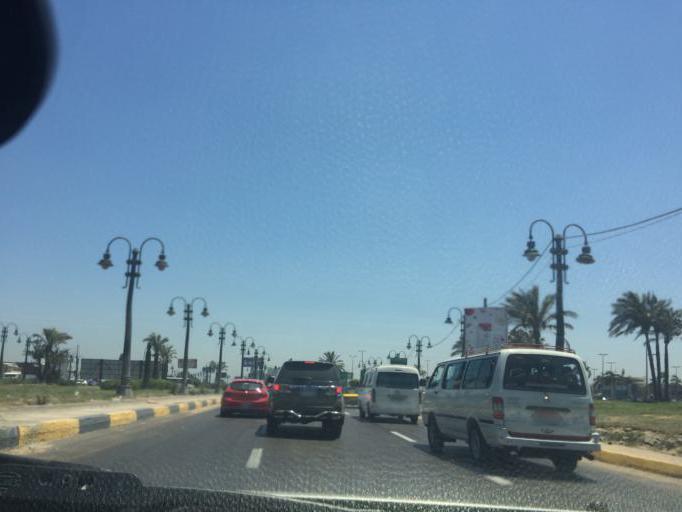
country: EG
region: Alexandria
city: Alexandria
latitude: 31.1707
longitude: 29.9339
